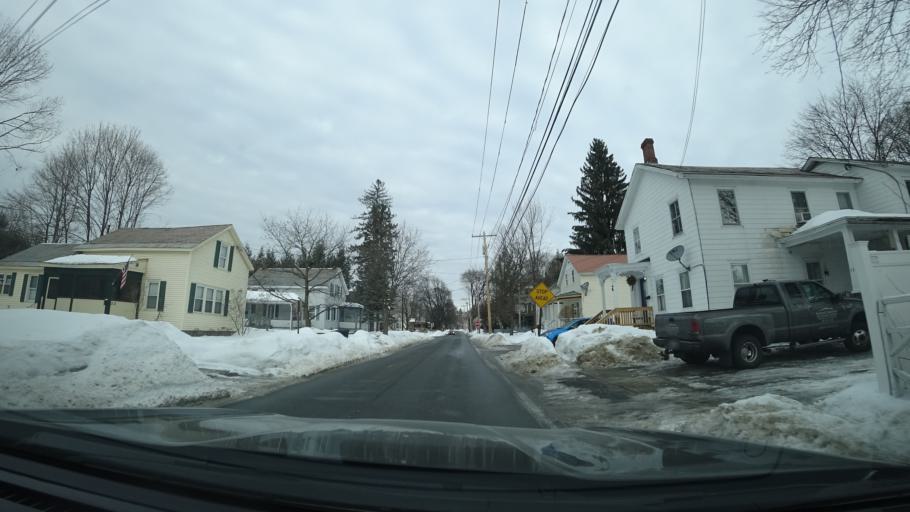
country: US
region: New York
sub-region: Warren County
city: Glens Falls
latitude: 43.3109
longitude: -73.6542
